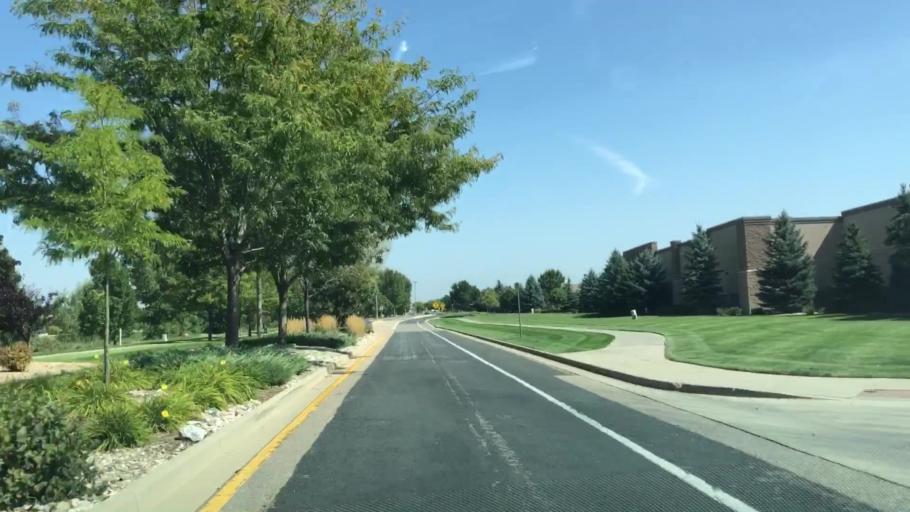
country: US
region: Colorado
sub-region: Larimer County
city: Loveland
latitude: 40.4104
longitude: -105.0094
